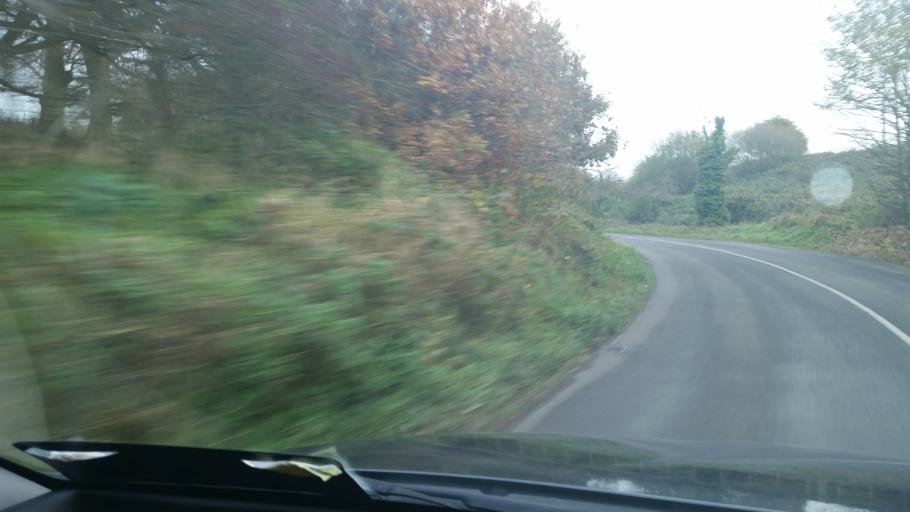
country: IE
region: Leinster
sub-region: Lu
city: Tullyallen
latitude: 53.6963
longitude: -6.4343
